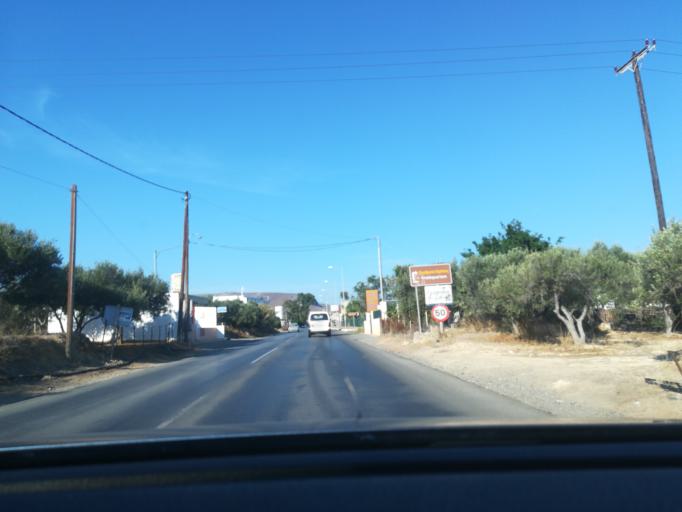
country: GR
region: Crete
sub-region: Nomos Irakleiou
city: Gournes
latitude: 35.3267
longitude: 25.2890
